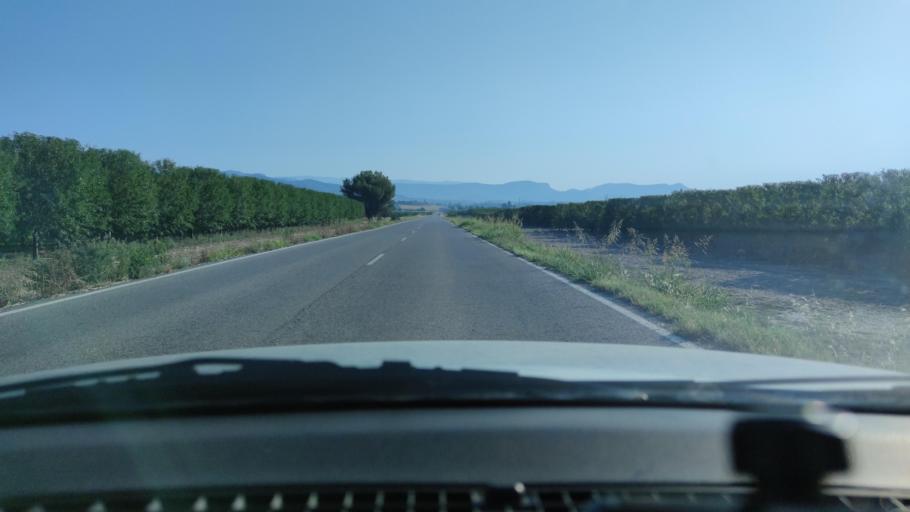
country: ES
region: Catalonia
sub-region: Provincia de Lleida
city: Balaguer
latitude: 41.8136
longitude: 0.8337
